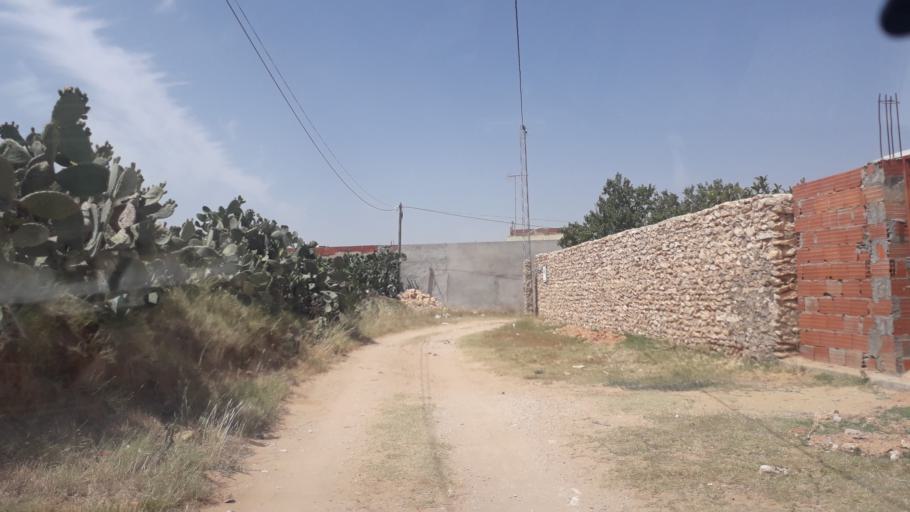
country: TN
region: Safaqis
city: Al Qarmadah
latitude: 34.8338
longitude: 10.7671
